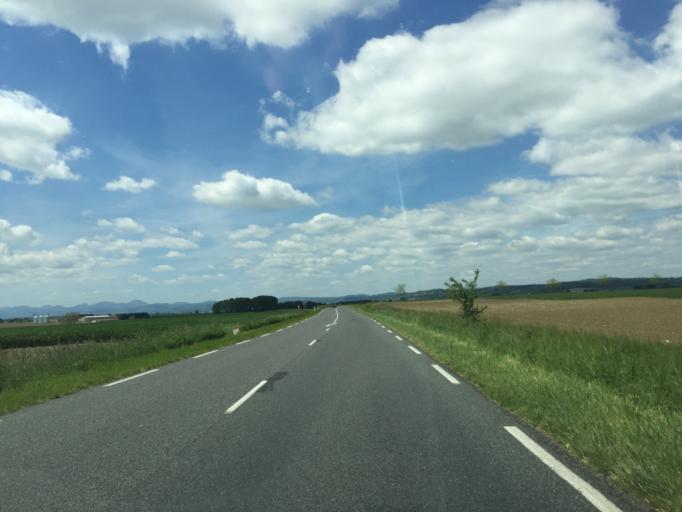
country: FR
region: Auvergne
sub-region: Departement du Puy-de-Dome
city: Aigueperse
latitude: 46.0235
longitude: 3.2367
